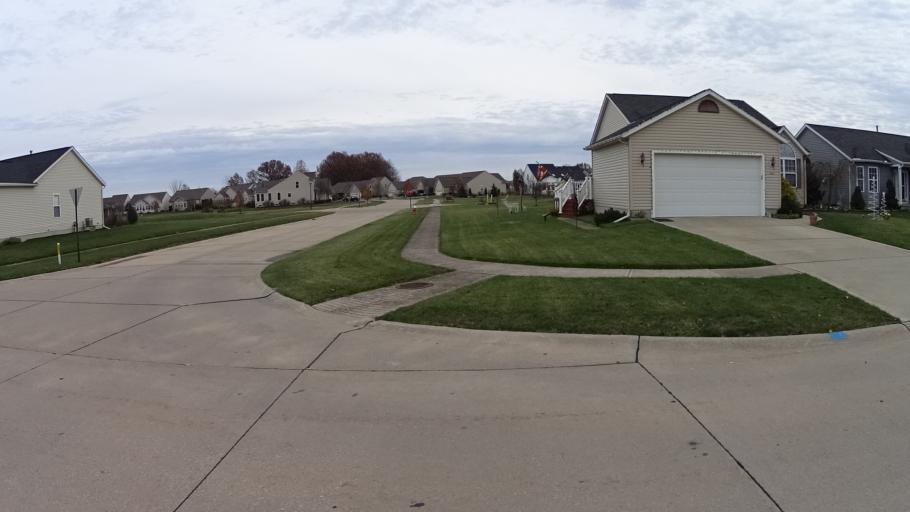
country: US
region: Ohio
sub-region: Lorain County
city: North Ridgeville
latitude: 41.4041
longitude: -82.0429
